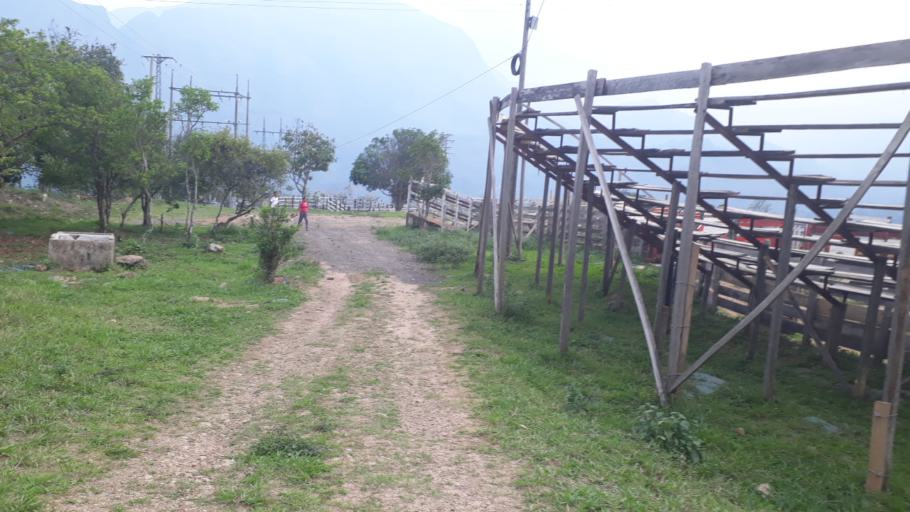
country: CO
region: Casanare
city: Nunchia
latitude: 5.6253
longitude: -72.4255
